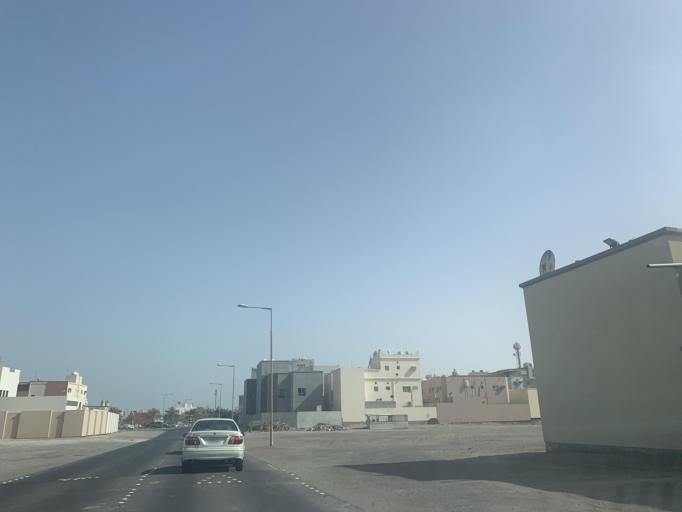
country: BH
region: Northern
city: Sitrah
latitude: 26.1657
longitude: 50.6232
